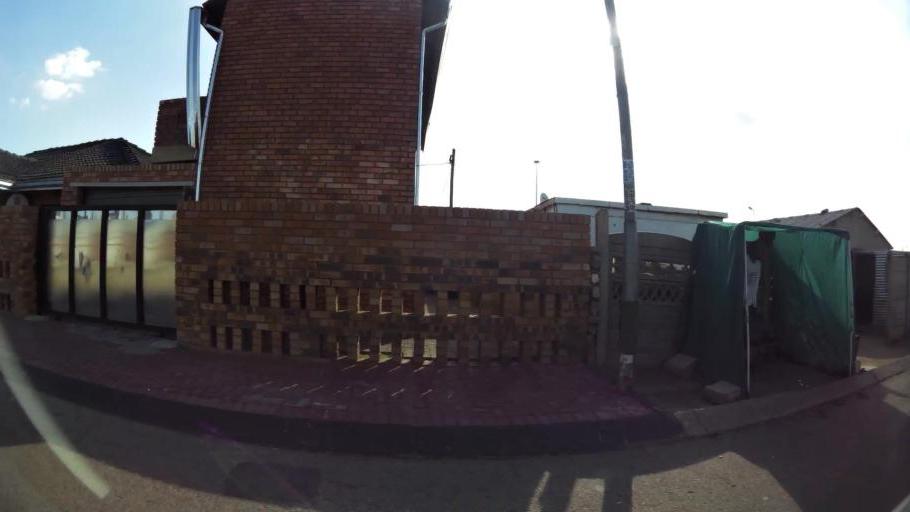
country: ZA
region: Gauteng
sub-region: City of Johannesburg Metropolitan Municipality
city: Soweto
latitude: -26.2584
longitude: 27.9067
